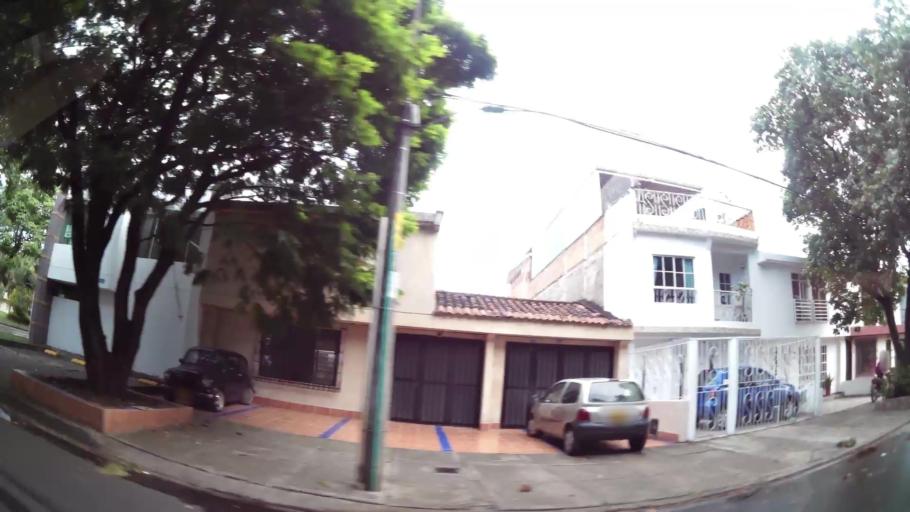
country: CO
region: Valle del Cauca
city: Cali
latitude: 3.4825
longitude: -76.5158
